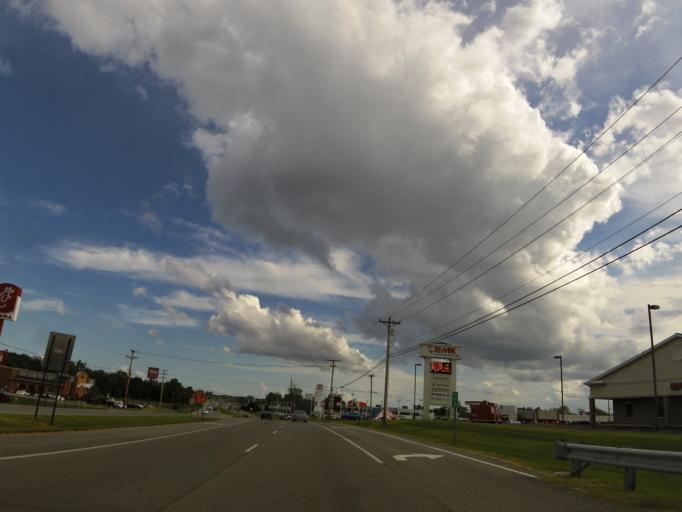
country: US
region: Kentucky
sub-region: Christian County
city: Hopkinsville
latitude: 36.8251
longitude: -87.4737
